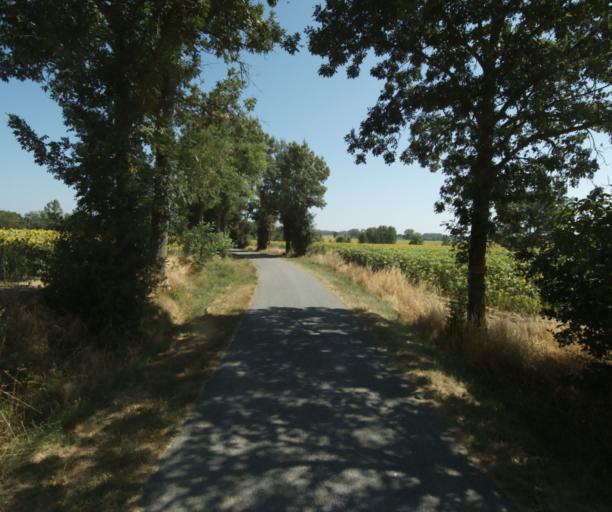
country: FR
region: Midi-Pyrenees
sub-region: Departement du Tarn
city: Puylaurens
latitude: 43.5249
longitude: 1.9572
